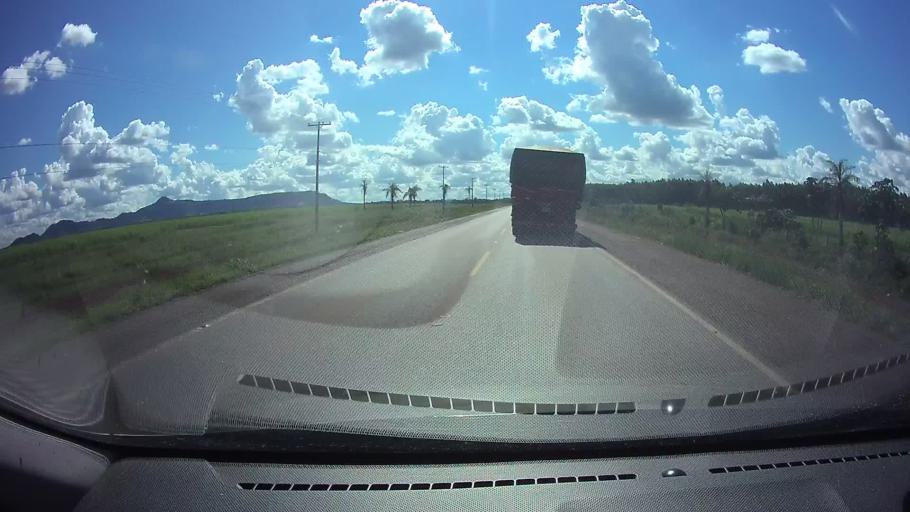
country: PY
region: Guaira
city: Coronel Martinez
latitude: -25.7616
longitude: -56.7419
